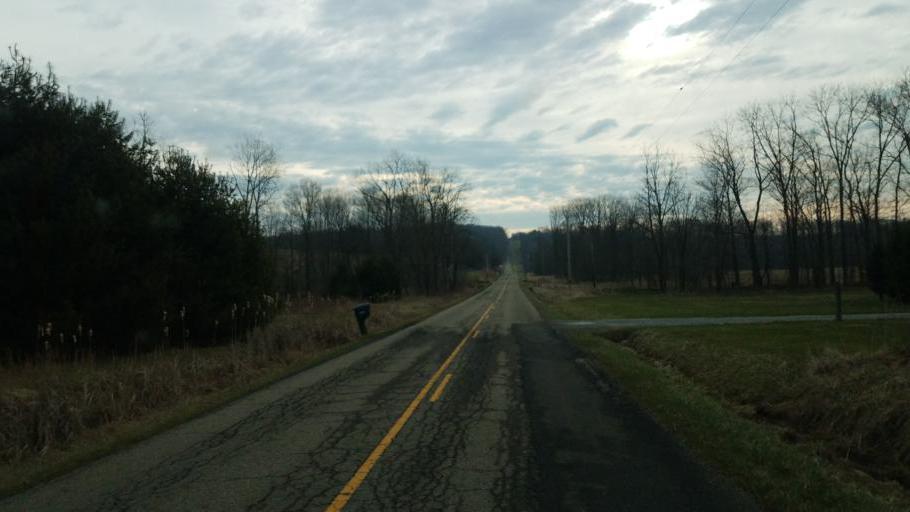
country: US
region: Ohio
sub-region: Knox County
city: Fredericktown
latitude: 40.4946
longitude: -82.4239
